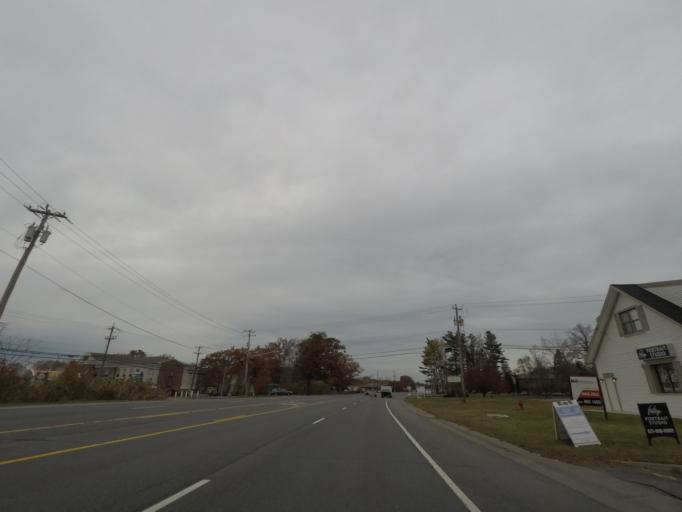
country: US
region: New York
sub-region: Saratoga County
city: Country Knolls
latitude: 42.8676
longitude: -73.7723
